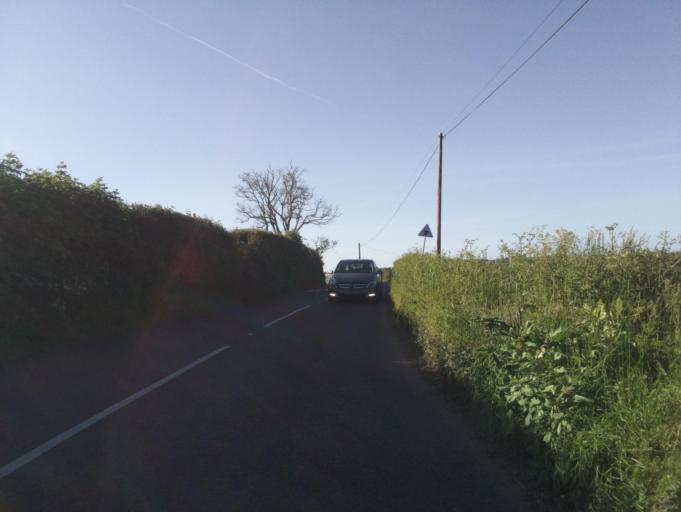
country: GB
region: England
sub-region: Somerset
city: Crewkerne
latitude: 50.8338
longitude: -2.8585
